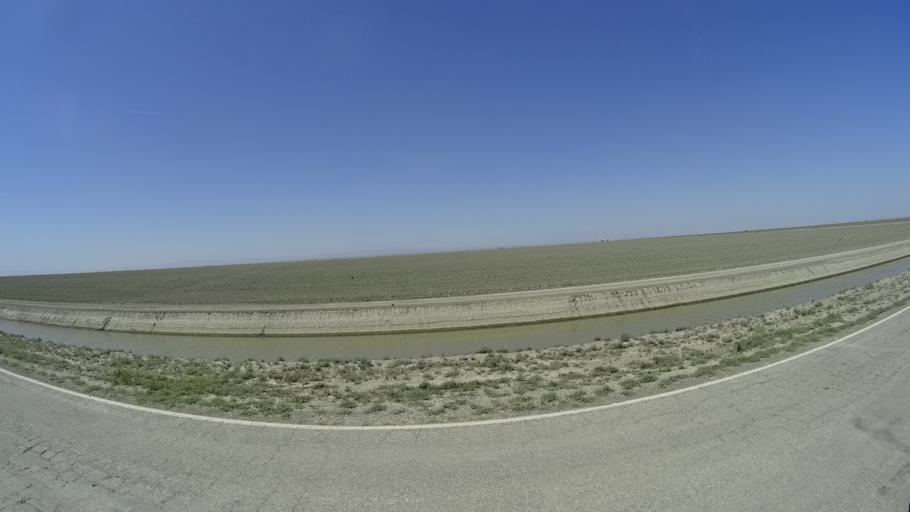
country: US
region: California
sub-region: Kings County
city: Corcoran
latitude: 36.0046
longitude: -119.6432
